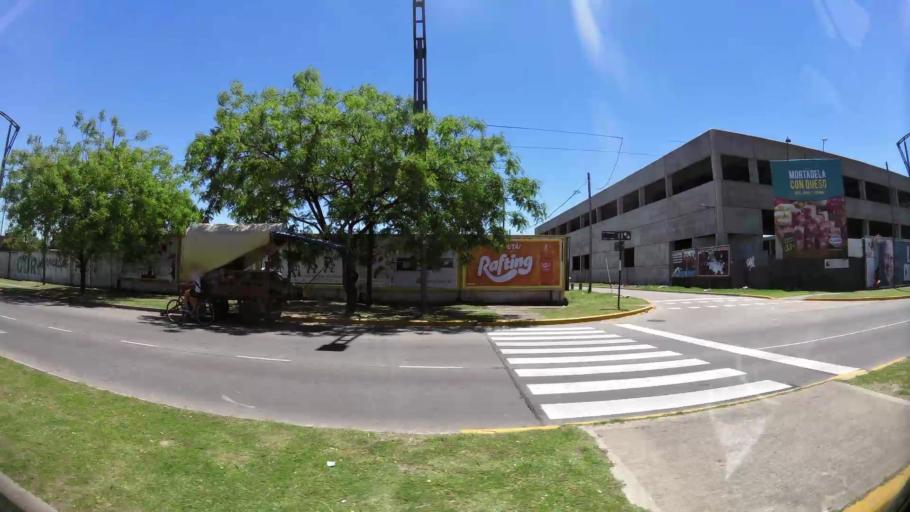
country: AR
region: Santa Fe
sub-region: Departamento de Rosario
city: Rosario
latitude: -32.9483
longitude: -60.7064
